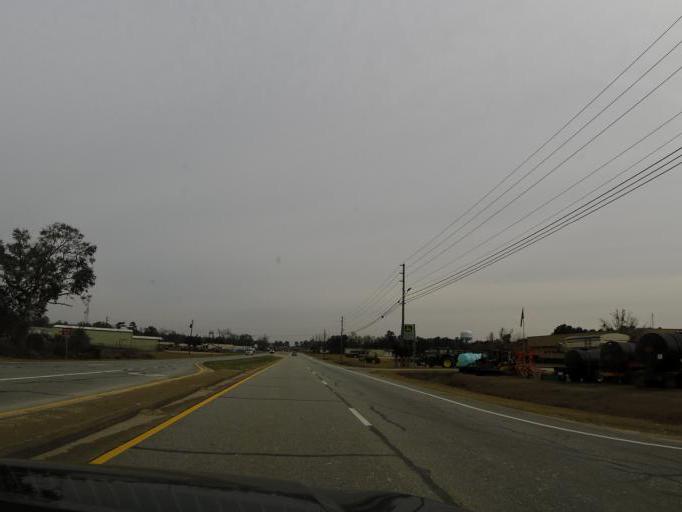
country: US
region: Georgia
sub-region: Decatur County
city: Bainbridge
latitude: 30.9227
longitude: -84.6092
